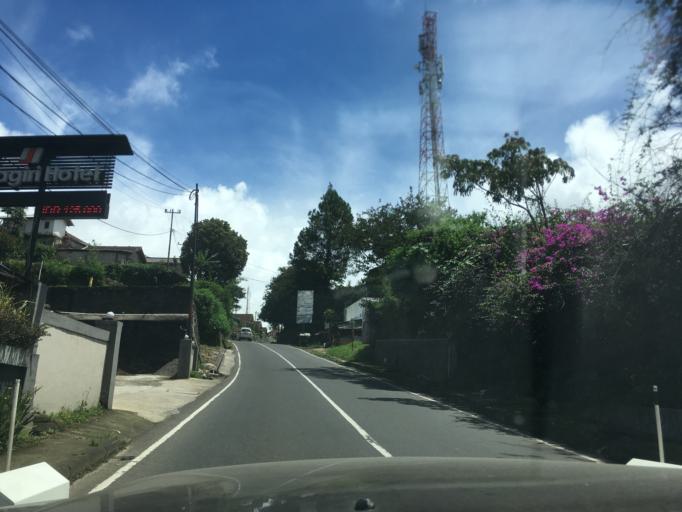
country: ID
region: West Java
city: Lembang
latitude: -6.7916
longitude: 107.6545
